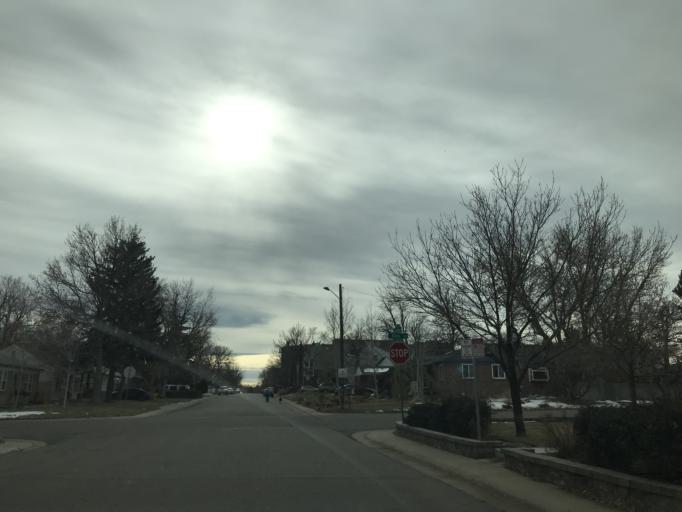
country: US
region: Colorado
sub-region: Arapahoe County
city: Glendale
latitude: 39.7340
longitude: -104.9184
